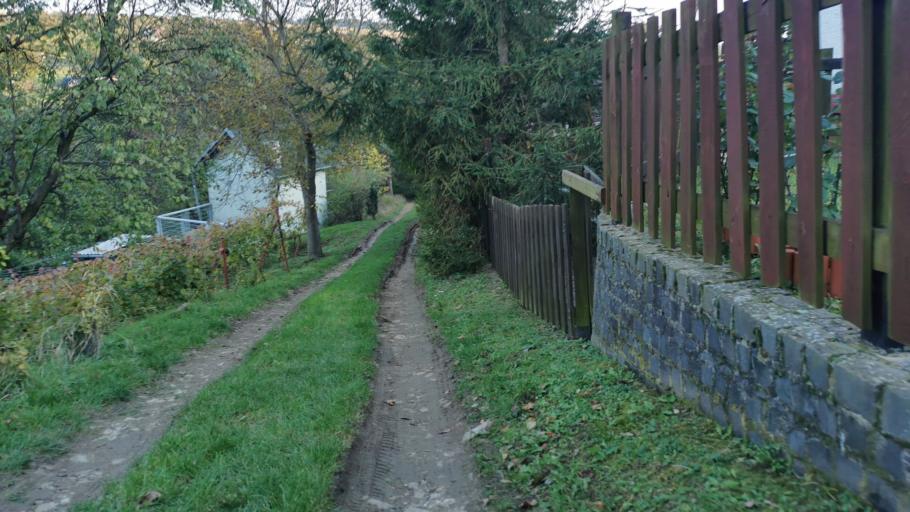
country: SK
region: Trnavsky
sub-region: Okres Skalica
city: Skalica
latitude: 48.8326
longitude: 17.2501
